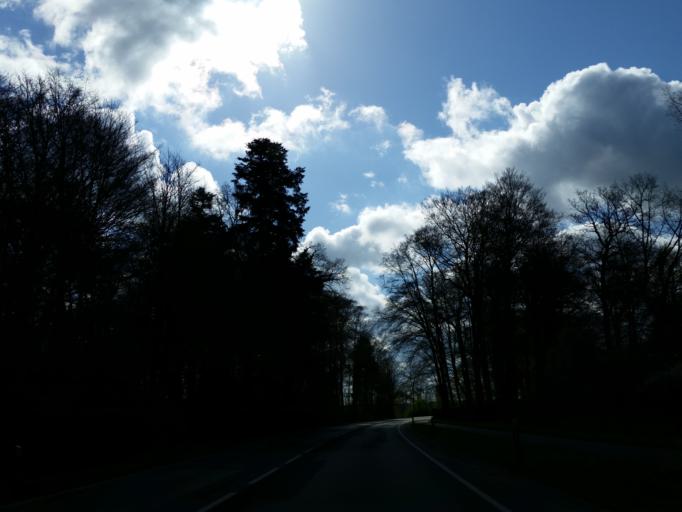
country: DE
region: Lower Saxony
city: Botersen
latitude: 53.1380
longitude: 9.3579
